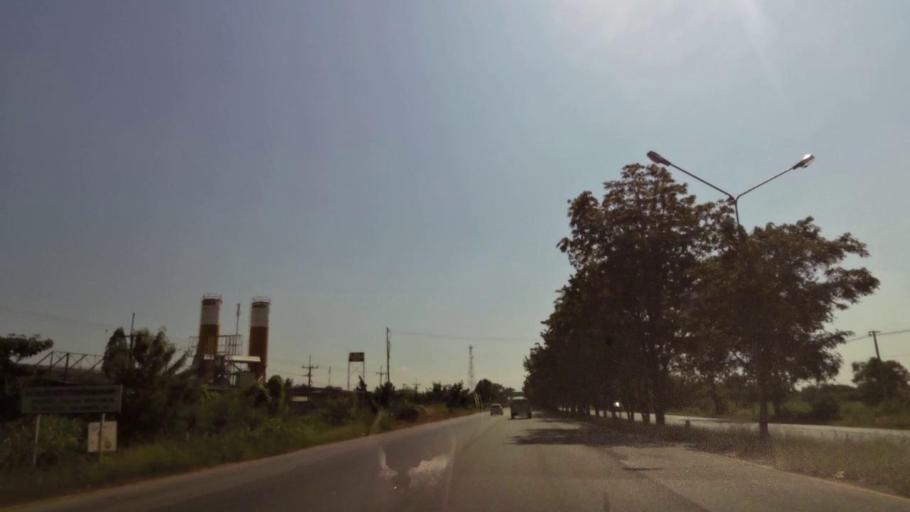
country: TH
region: Nakhon Sawan
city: Kao Liao
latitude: 15.8752
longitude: 100.1162
